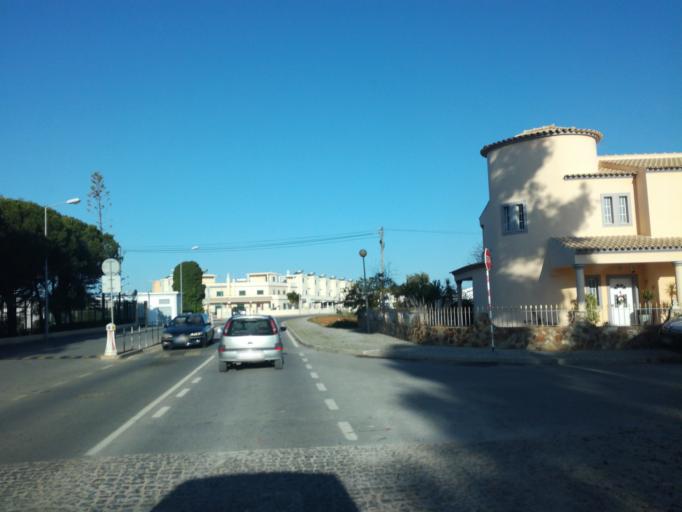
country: PT
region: Faro
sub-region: Olhao
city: Laranjeiro
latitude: 37.0572
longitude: -7.7616
